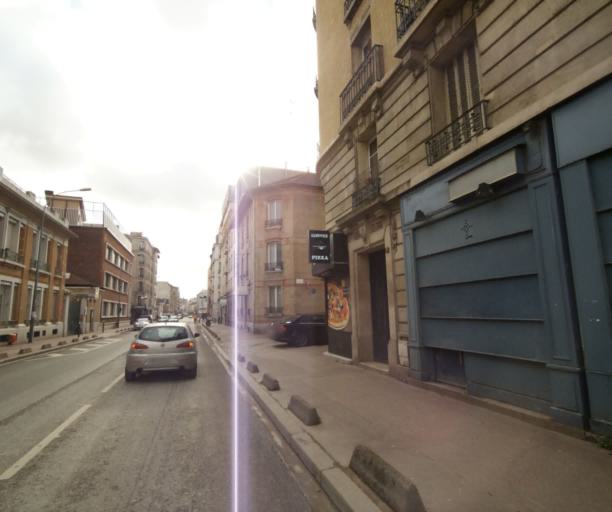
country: FR
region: Ile-de-France
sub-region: Paris
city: Saint-Ouen
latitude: 48.9082
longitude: 2.3402
